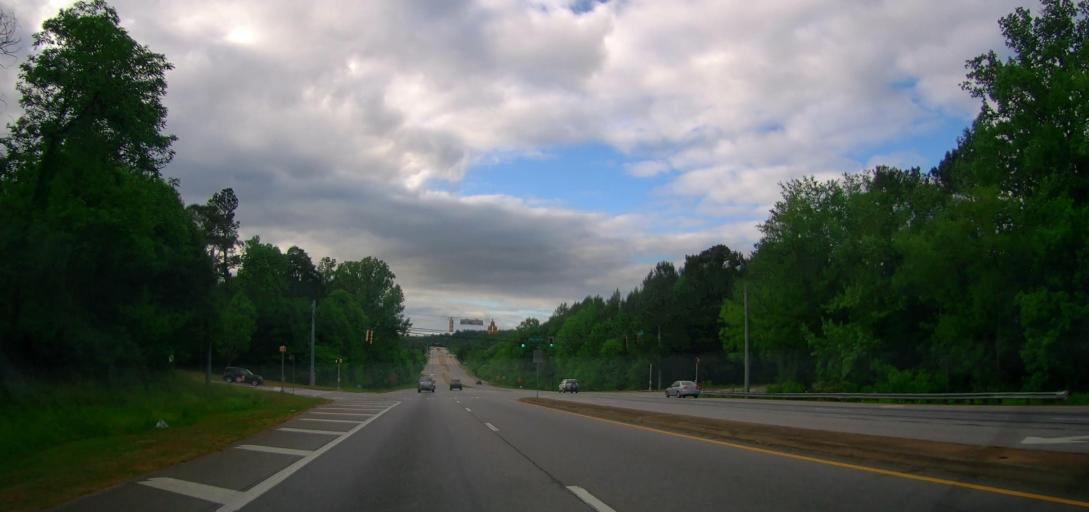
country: US
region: Georgia
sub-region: Oconee County
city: Watkinsville
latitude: 33.9082
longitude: -83.4043
